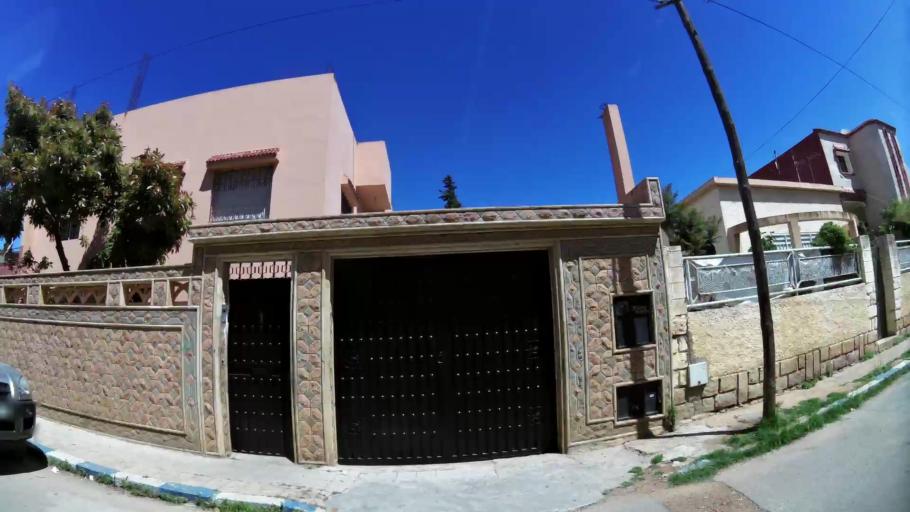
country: MA
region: Meknes-Tafilalet
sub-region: Meknes
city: Meknes
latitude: 33.9037
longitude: -5.5261
